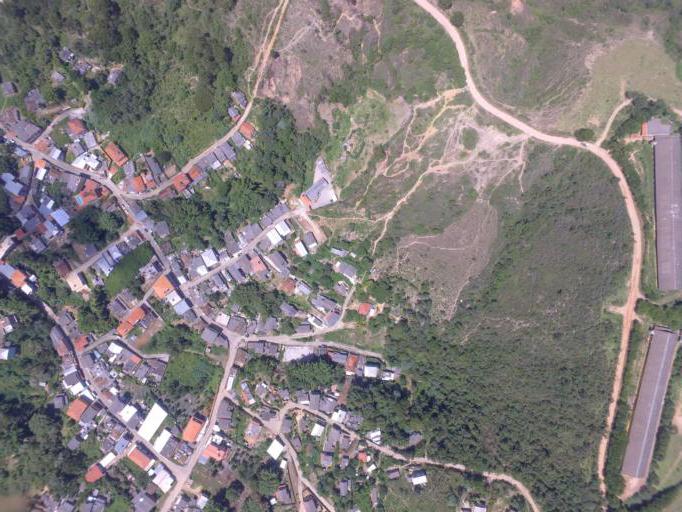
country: BR
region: Minas Gerais
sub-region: Tiradentes
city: Tiradentes
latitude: -21.0526
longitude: -44.0770
